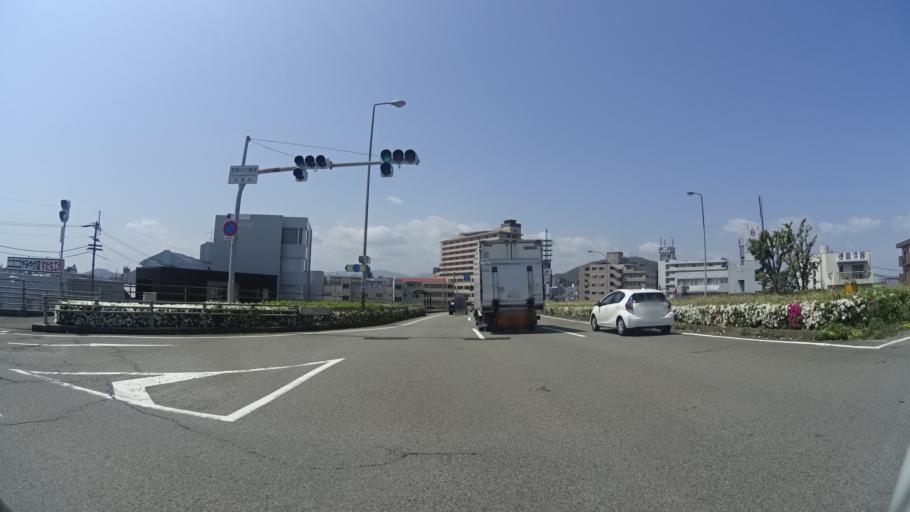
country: JP
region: Tokushima
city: Tokushima-shi
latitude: 34.0848
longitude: 134.5650
